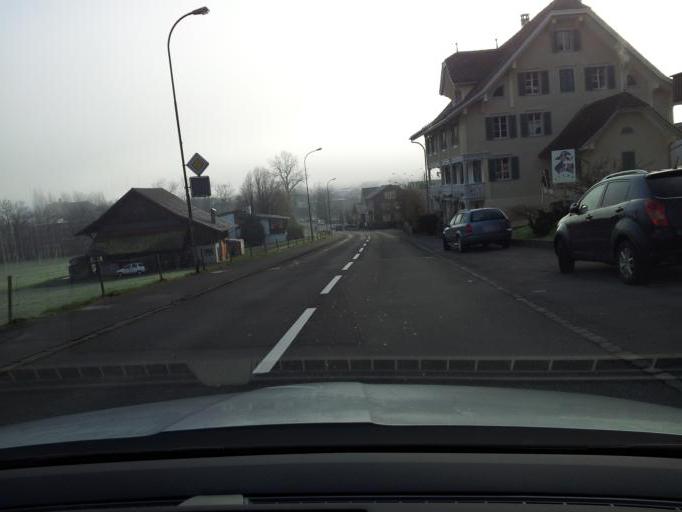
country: CH
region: Obwalden
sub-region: Obwalden
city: Sarnen
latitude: 46.8931
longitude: 8.2386
